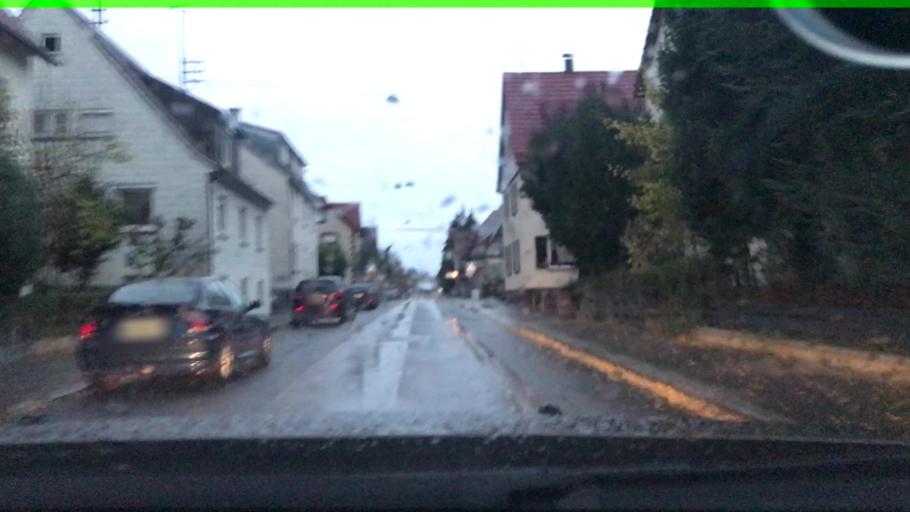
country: DE
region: Baden-Wuerttemberg
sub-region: Regierungsbezirk Stuttgart
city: Winnenden
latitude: 48.8730
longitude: 9.4030
